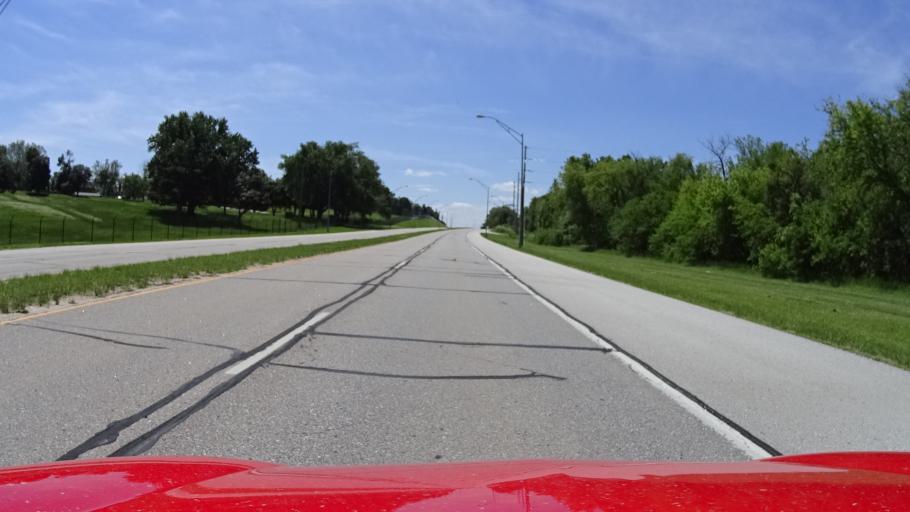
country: US
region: Nebraska
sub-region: Sarpy County
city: Offutt Air Force Base
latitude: 41.1273
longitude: -95.9265
